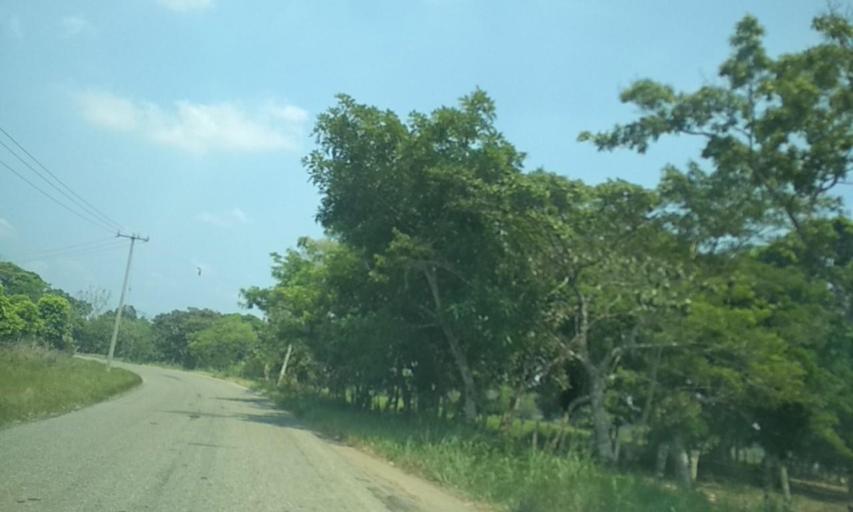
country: MX
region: Tabasco
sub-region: Huimanguillo
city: C-41 (Licenciado Carlos A. Madrazo)
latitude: 17.8297
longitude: -93.5111
